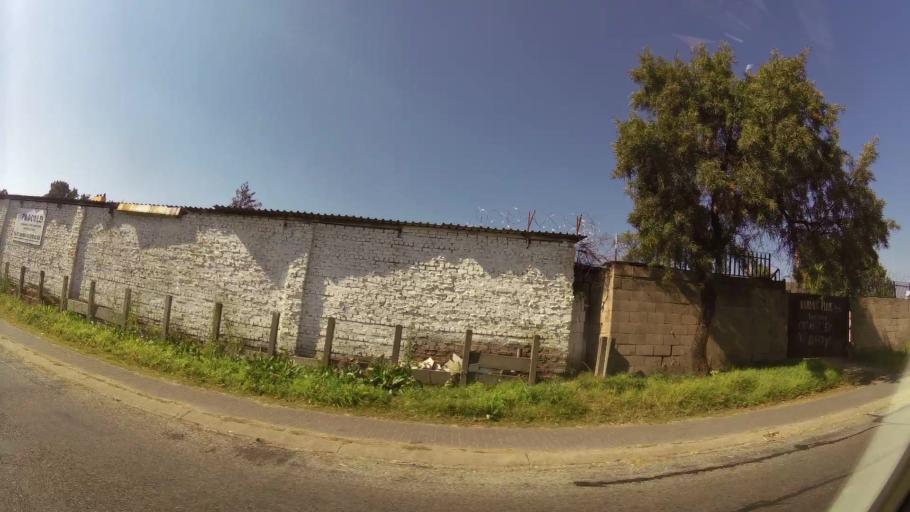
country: ZA
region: Gauteng
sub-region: City of Johannesburg Metropolitan Municipality
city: Johannesburg
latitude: -26.2436
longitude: 28.0283
